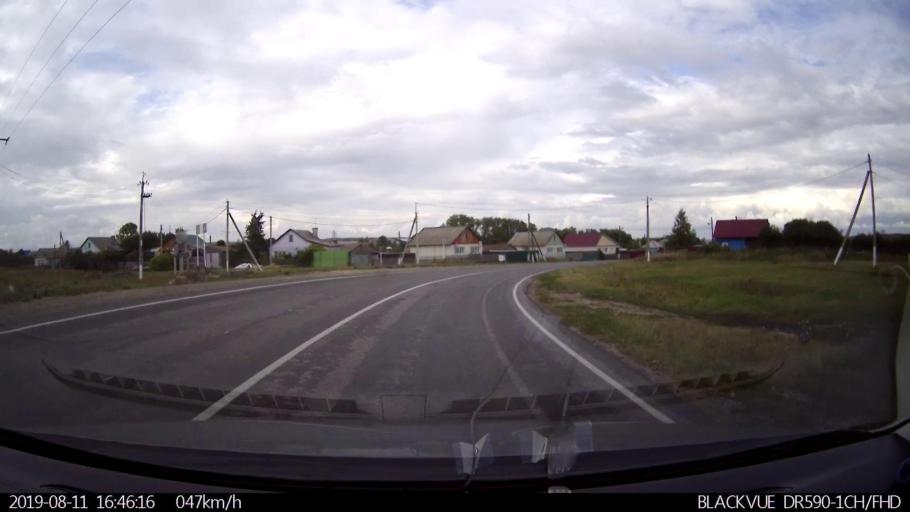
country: RU
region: Ulyanovsk
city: Mayna
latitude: 54.1970
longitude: 47.6873
